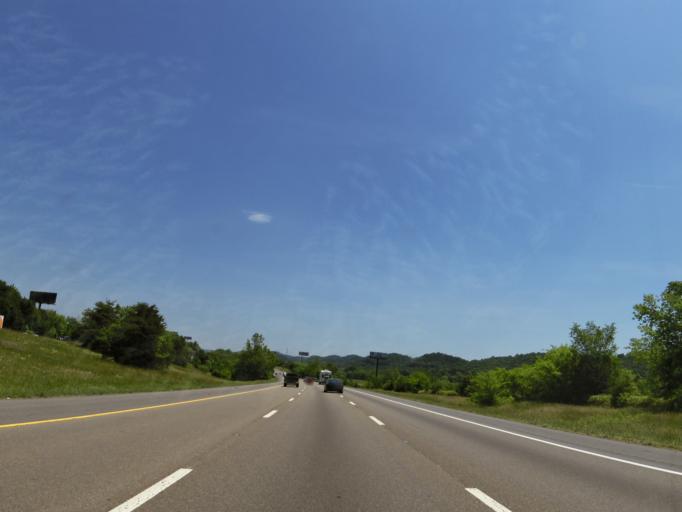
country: US
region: Tennessee
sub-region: Sevier County
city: Sevierville
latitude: 35.9853
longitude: -83.5885
